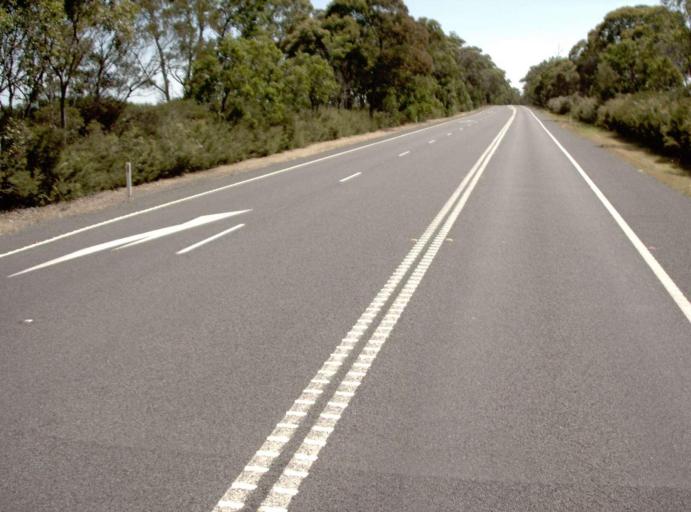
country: AU
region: Victoria
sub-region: Wellington
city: Sale
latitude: -37.9394
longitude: 147.1494
